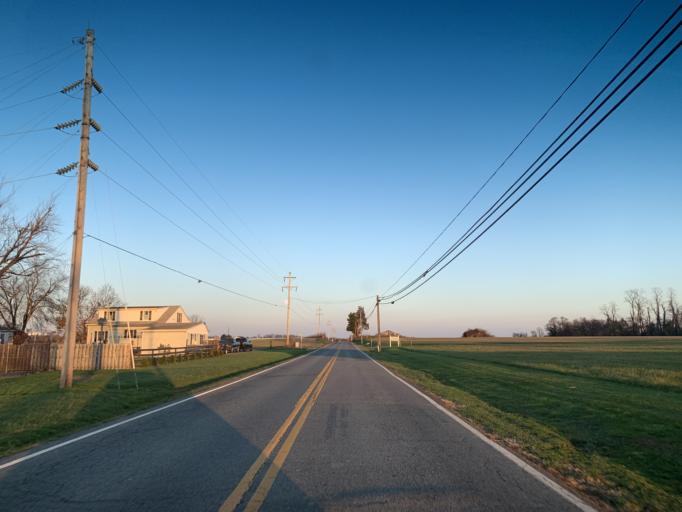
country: US
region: Maryland
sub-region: Cecil County
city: Charlestown
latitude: 39.4102
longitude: -75.9181
